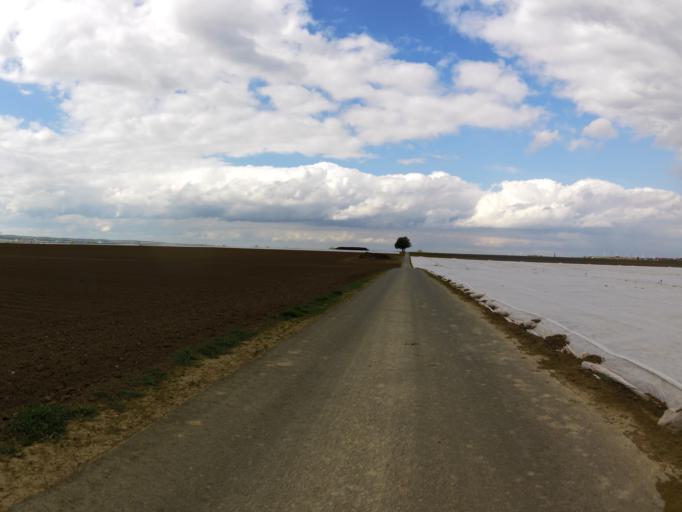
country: DE
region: Bavaria
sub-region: Regierungsbezirk Unterfranken
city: Oberpleichfeld
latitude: 49.8637
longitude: 10.0815
